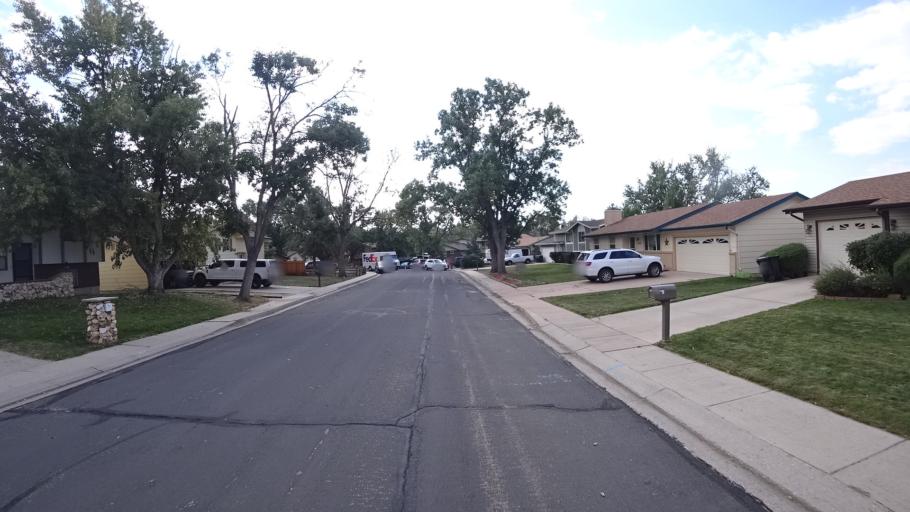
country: US
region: Colorado
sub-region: El Paso County
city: Cimarron Hills
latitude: 38.8801
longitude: -104.7439
